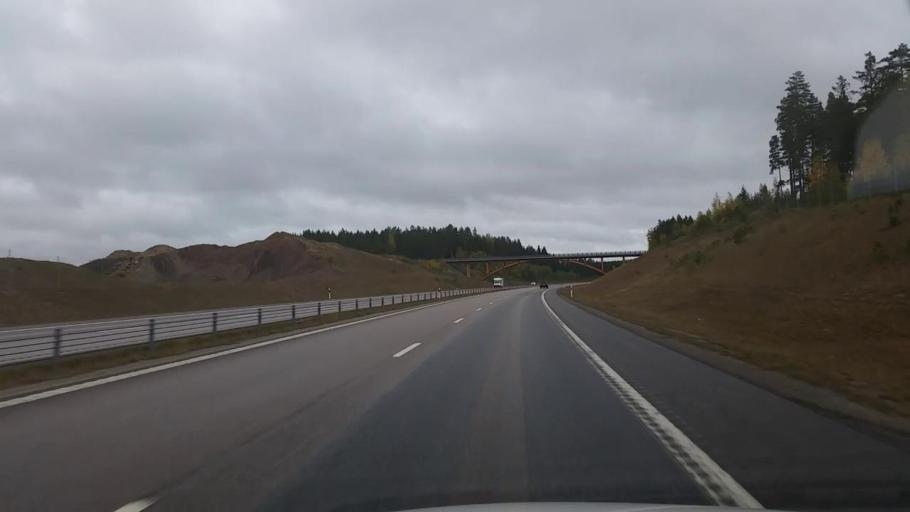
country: SE
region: Uppsala
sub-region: Osthammars Kommun
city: Bjorklinge
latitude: 60.1182
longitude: 17.5486
